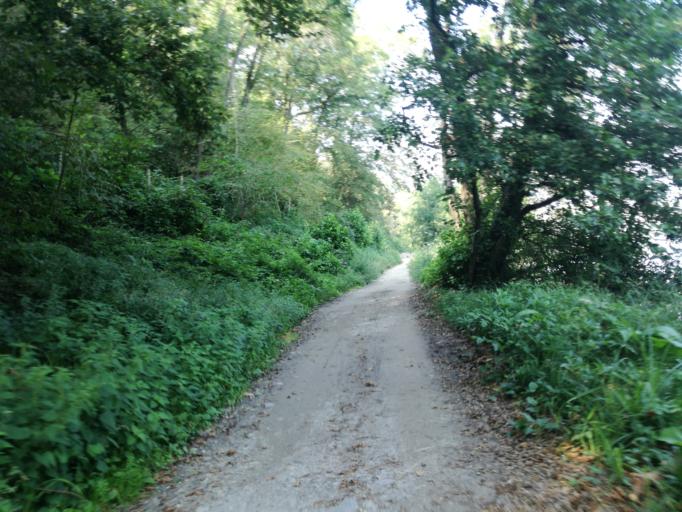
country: IT
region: Lombardy
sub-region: Provincia di Lecco
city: Arlate
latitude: 45.7213
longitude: 9.4487
